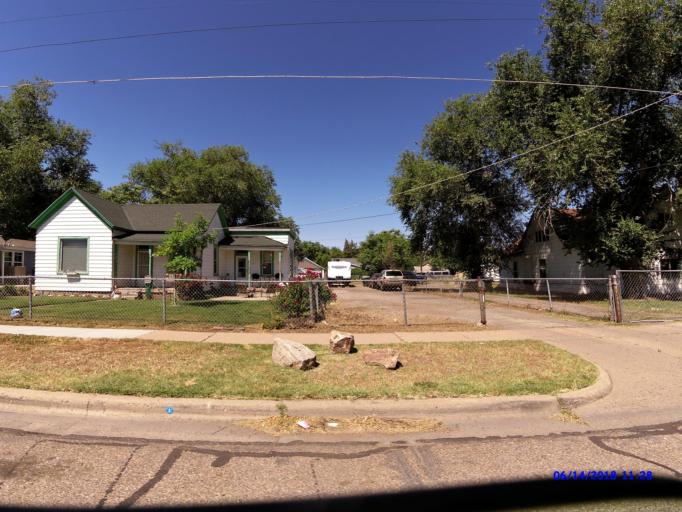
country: US
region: Utah
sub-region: Weber County
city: Ogden
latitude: 41.2215
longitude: -111.9914
